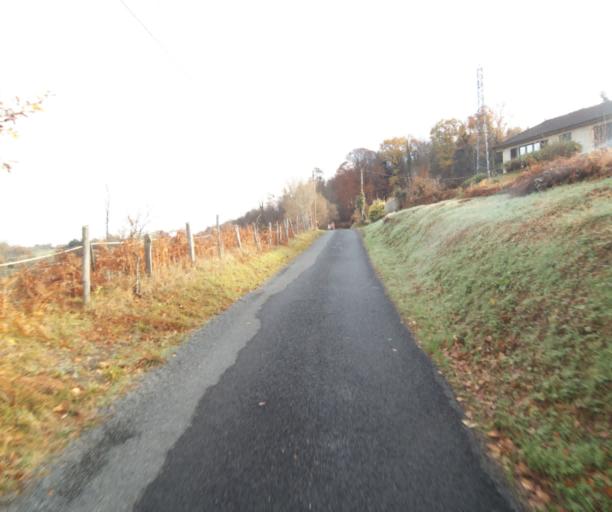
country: FR
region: Limousin
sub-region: Departement de la Correze
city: Chameyrat
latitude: 45.2251
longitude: 1.7244
